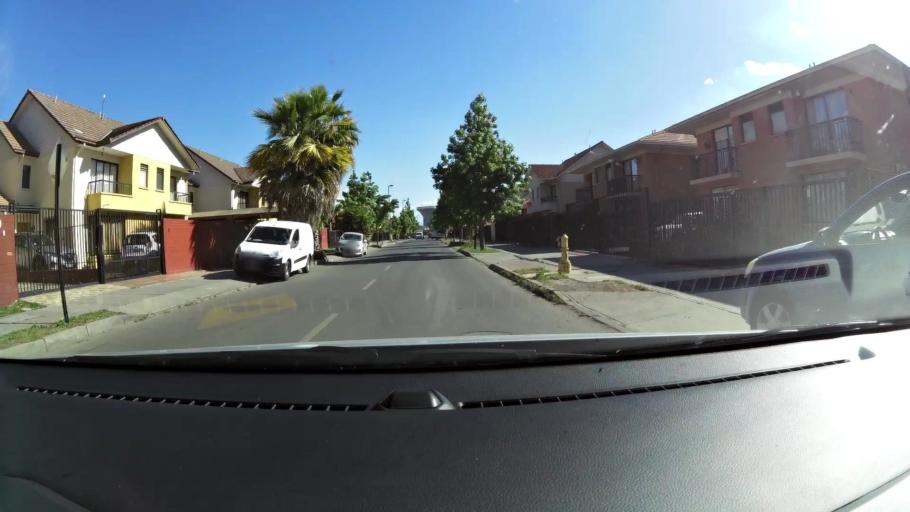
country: CL
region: Santiago Metropolitan
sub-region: Provincia de Maipo
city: San Bernardo
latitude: -33.5610
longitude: -70.7809
